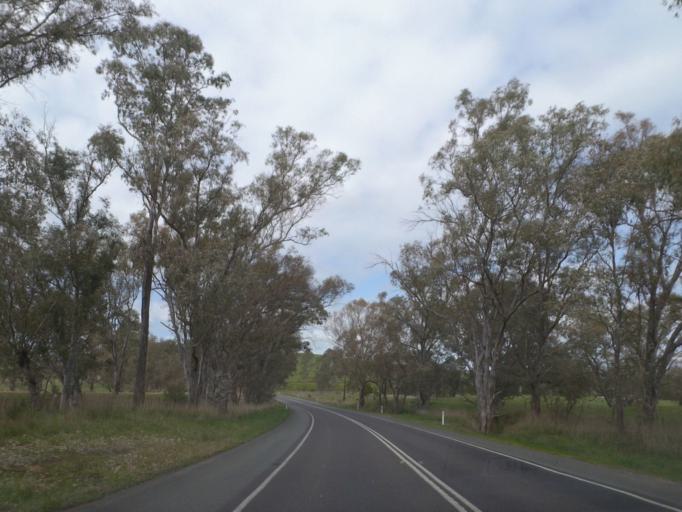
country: AU
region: Victoria
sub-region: Murrindindi
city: Kinglake West
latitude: -37.1629
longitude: 145.2922
